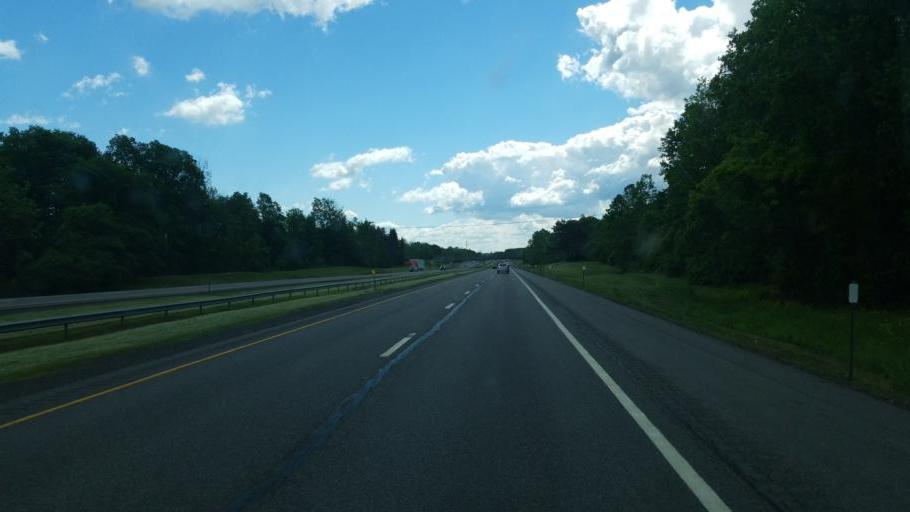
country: US
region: New York
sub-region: Madison County
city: Canastota
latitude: 43.0918
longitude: -75.7827
